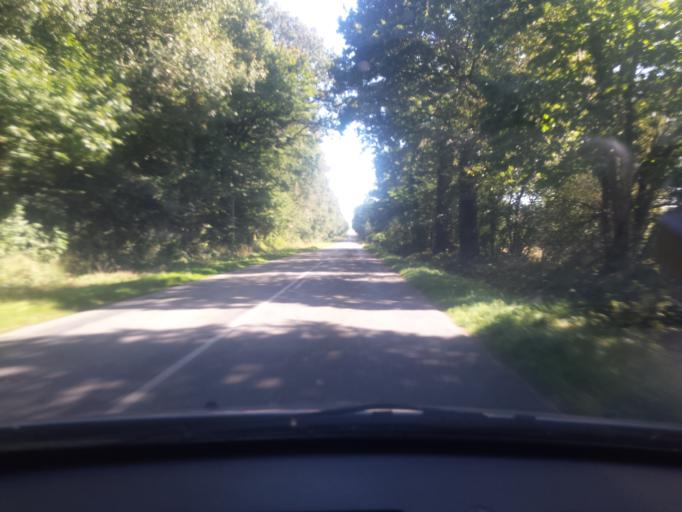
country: FR
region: Brittany
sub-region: Departement du Morbihan
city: Cleguerec
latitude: 48.1093
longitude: -3.1142
